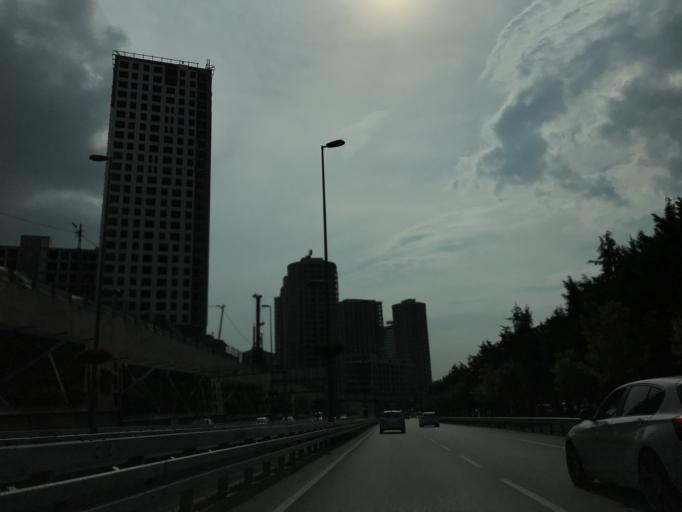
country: TR
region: Istanbul
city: UEskuedar
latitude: 40.9958
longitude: 29.0518
